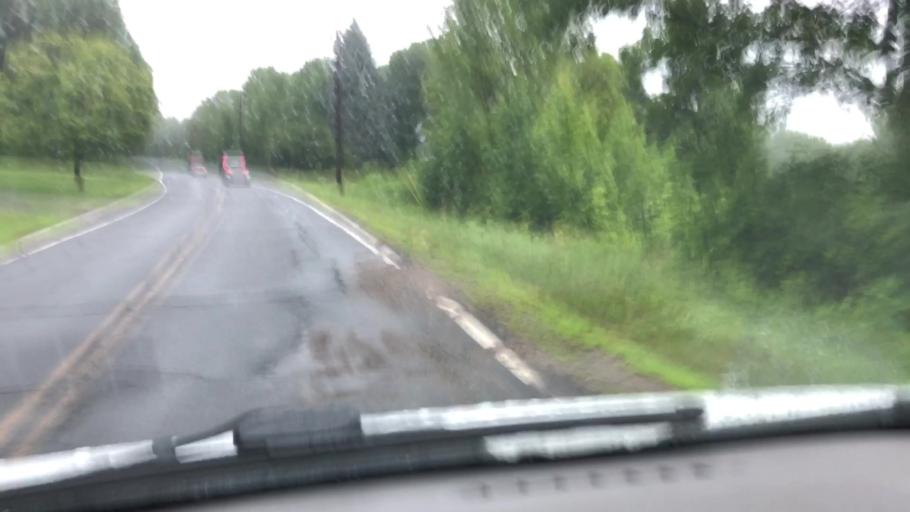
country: US
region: Massachusetts
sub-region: Hampshire County
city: Chesterfield
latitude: 42.4243
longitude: -72.9462
